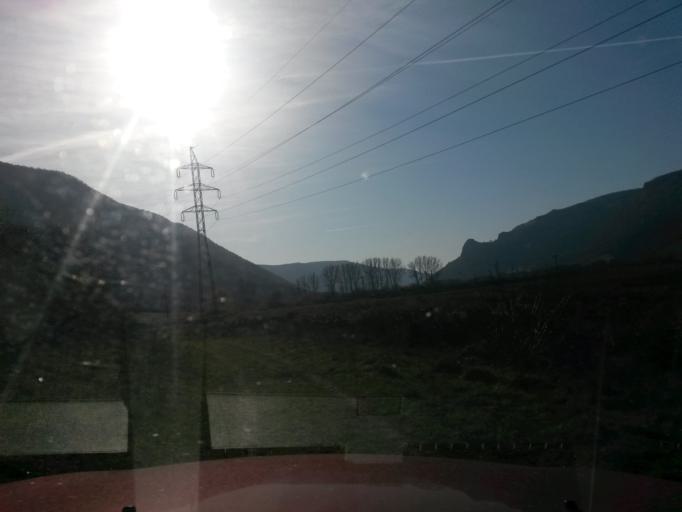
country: SK
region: Kosicky
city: Roznava
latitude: 48.5933
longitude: 20.4833
